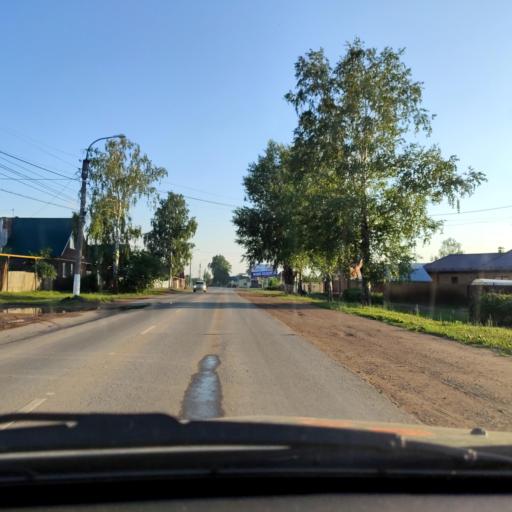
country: RU
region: Bashkortostan
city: Blagoveshchensk
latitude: 55.0383
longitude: 55.9965
